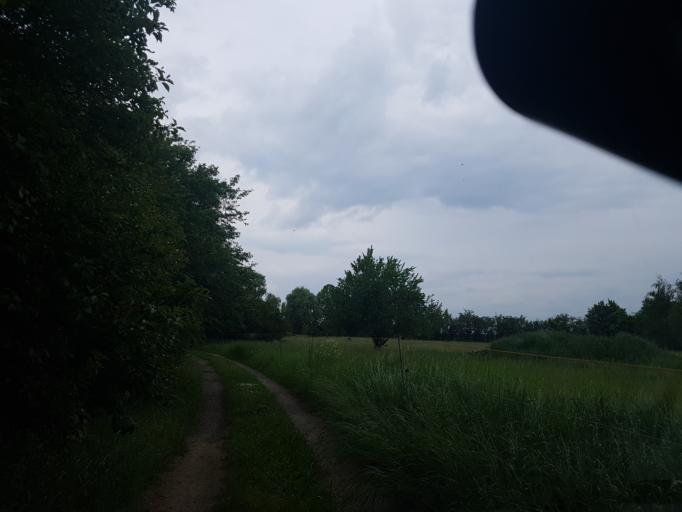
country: DE
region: Brandenburg
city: Finsterwalde
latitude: 51.6195
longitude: 13.7325
